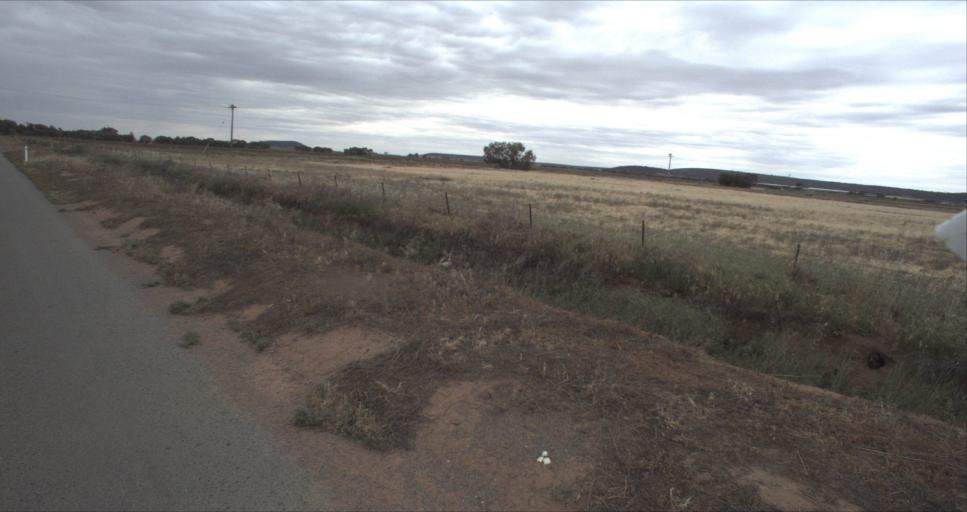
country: AU
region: New South Wales
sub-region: Leeton
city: Leeton
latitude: -34.4182
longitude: 146.3390
